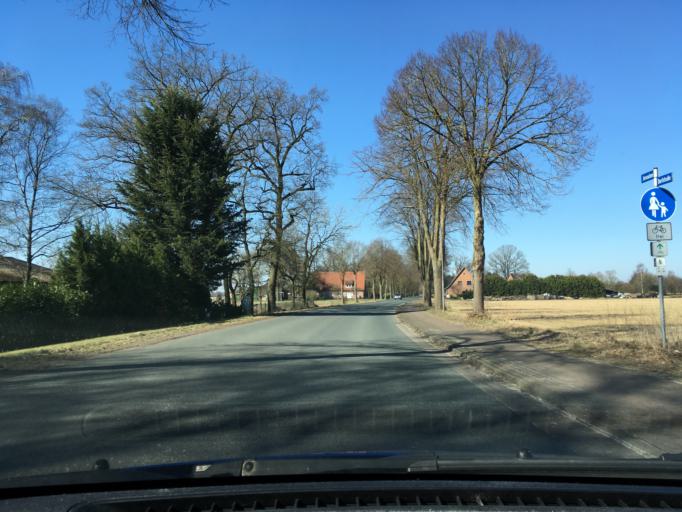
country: DE
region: Lower Saxony
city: Hemslingen
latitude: 53.0671
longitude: 9.6554
